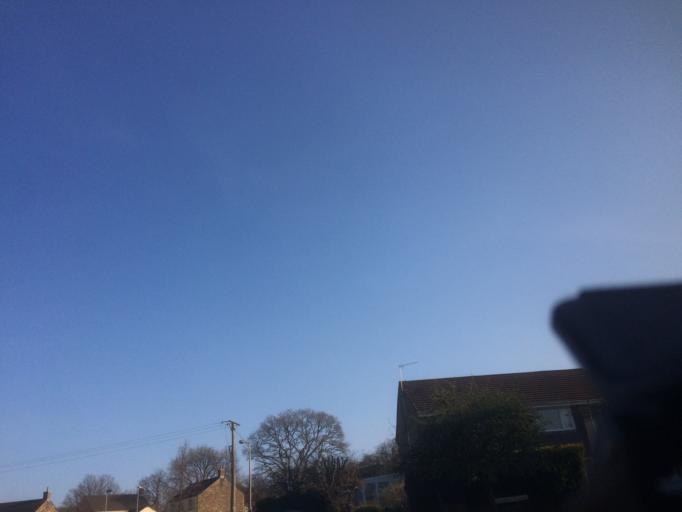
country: GB
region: England
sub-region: Devon
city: Tavistock
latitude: 50.5350
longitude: -4.1389
